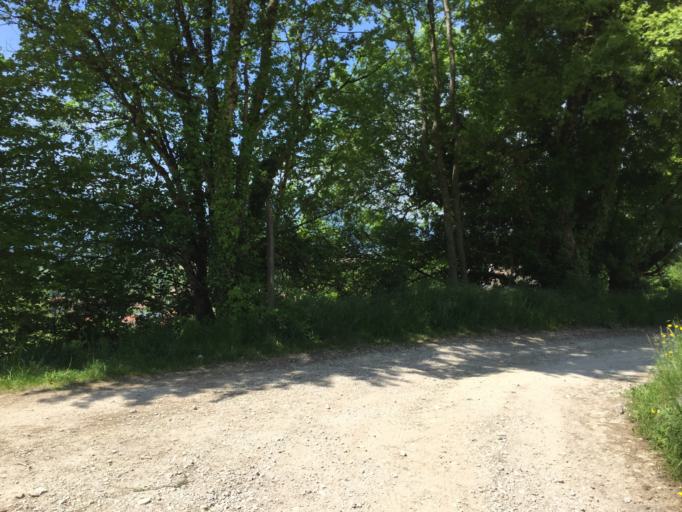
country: FR
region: Rhone-Alpes
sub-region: Departement de la Savoie
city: Mouxy
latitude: 45.6687
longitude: 5.9441
